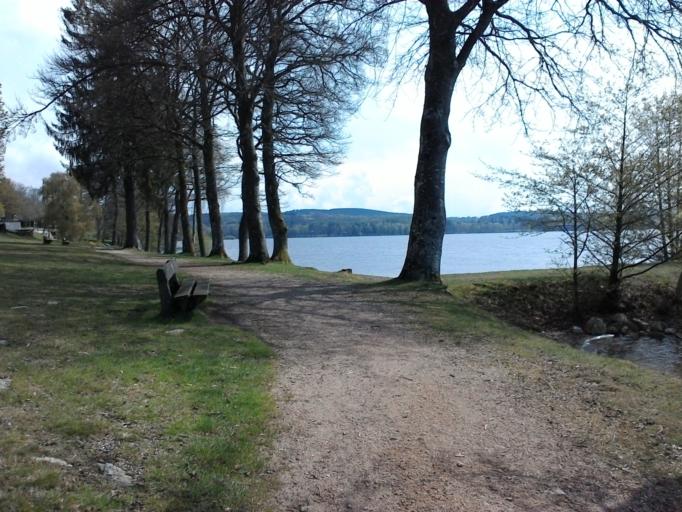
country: FR
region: Bourgogne
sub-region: Departement de la Nievre
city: Chateau-Chinon(Ville)
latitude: 47.1866
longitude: 4.0693
